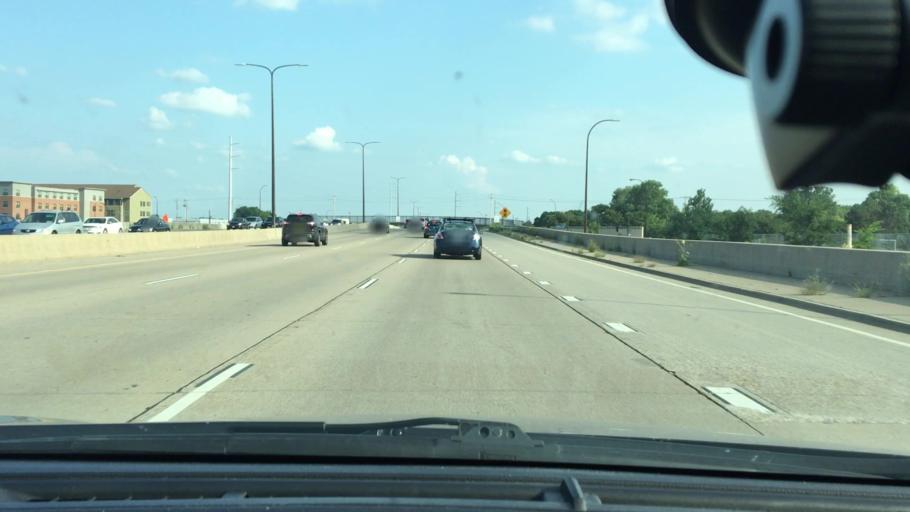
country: US
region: Minnesota
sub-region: Hennepin County
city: Minneapolis
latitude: 44.9611
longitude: -93.2481
